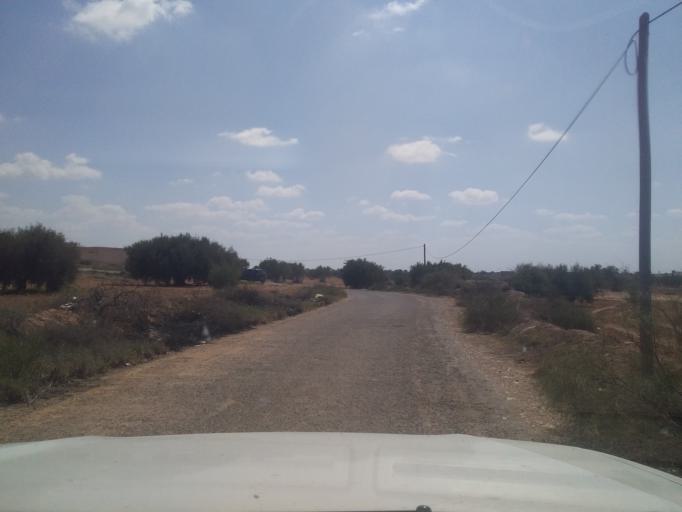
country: TN
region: Madanin
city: Medenine
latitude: 33.6107
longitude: 10.3093
